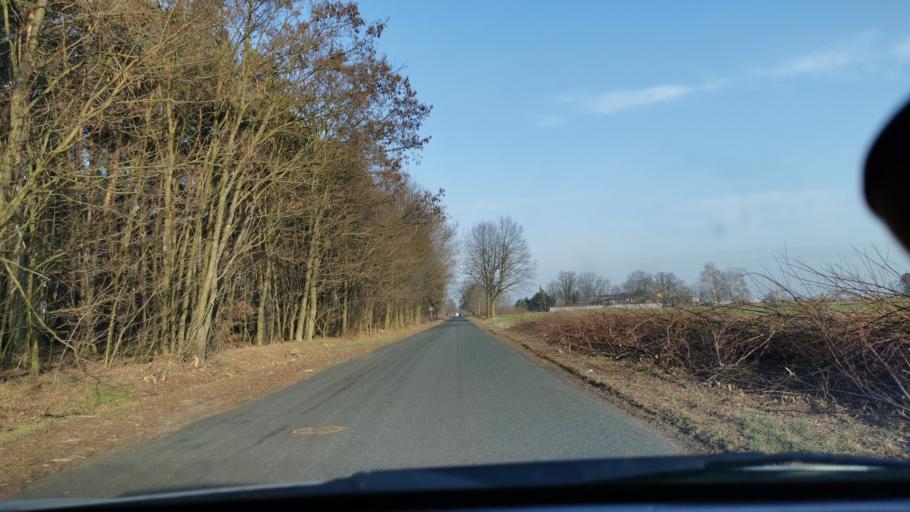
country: PL
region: Greater Poland Voivodeship
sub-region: Powiat kaliski
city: Opatowek
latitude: 51.6750
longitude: 18.2954
